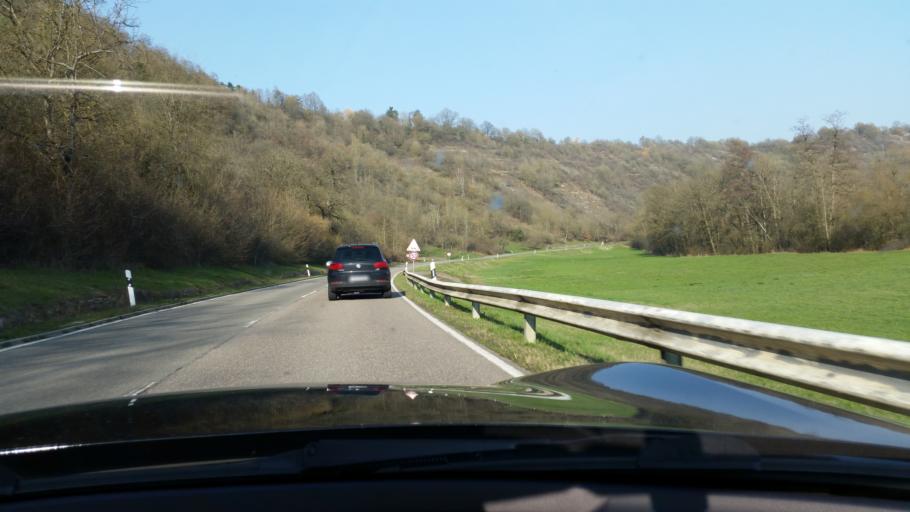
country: DE
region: Baden-Wuerttemberg
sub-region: Regierungsbezirk Stuttgart
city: Widdern
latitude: 49.3215
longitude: 9.3980
